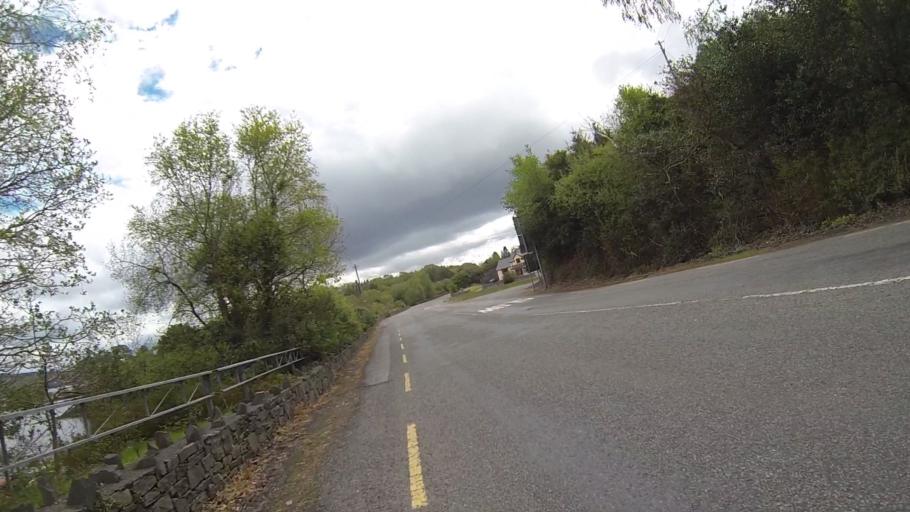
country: IE
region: Munster
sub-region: County Cork
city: Bantry
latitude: 51.7452
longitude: -9.5515
